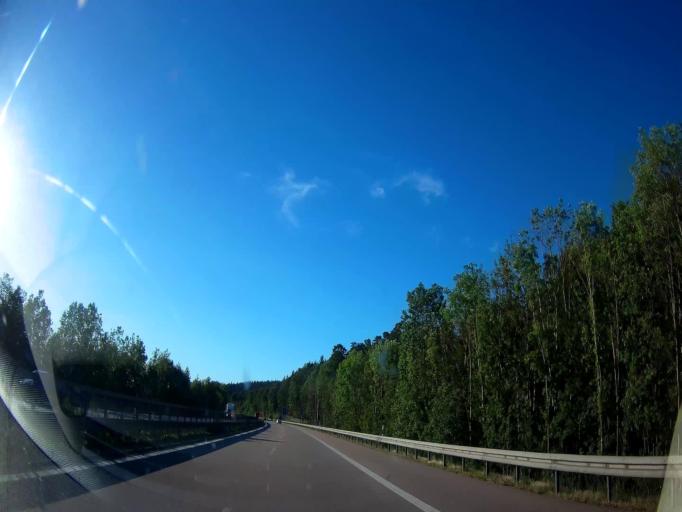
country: DE
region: Bavaria
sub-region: Upper Palatinate
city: Velburg
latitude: 49.2183
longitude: 11.6487
